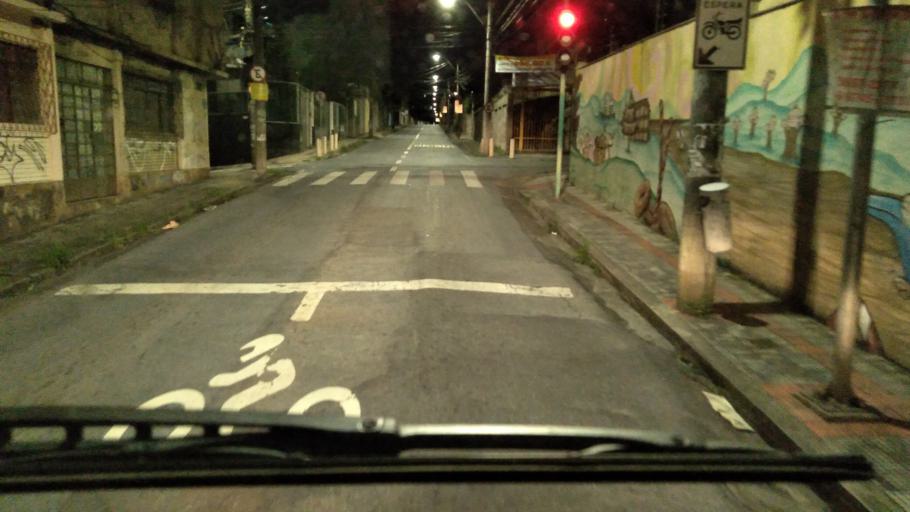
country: BR
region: Minas Gerais
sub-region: Belo Horizonte
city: Belo Horizonte
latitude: -19.9114
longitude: -43.9644
